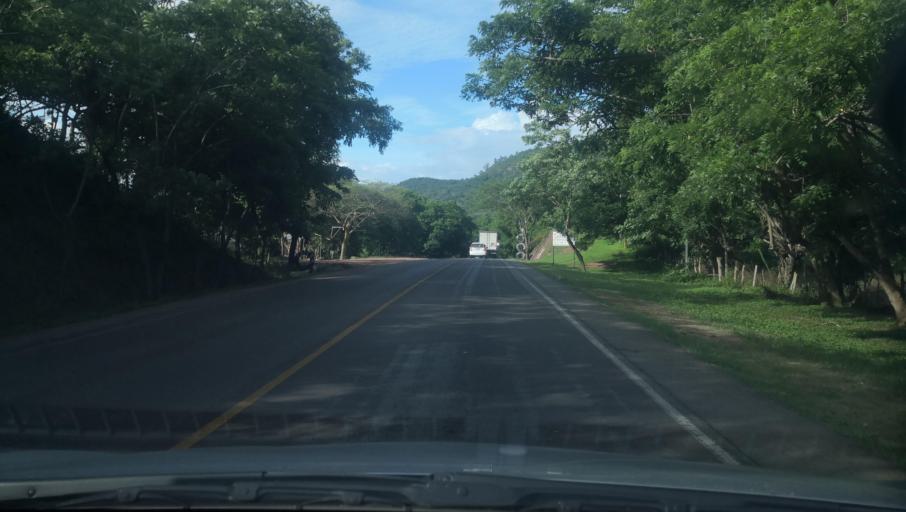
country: NI
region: Madriz
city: Totogalpa
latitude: 13.5742
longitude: -86.4815
